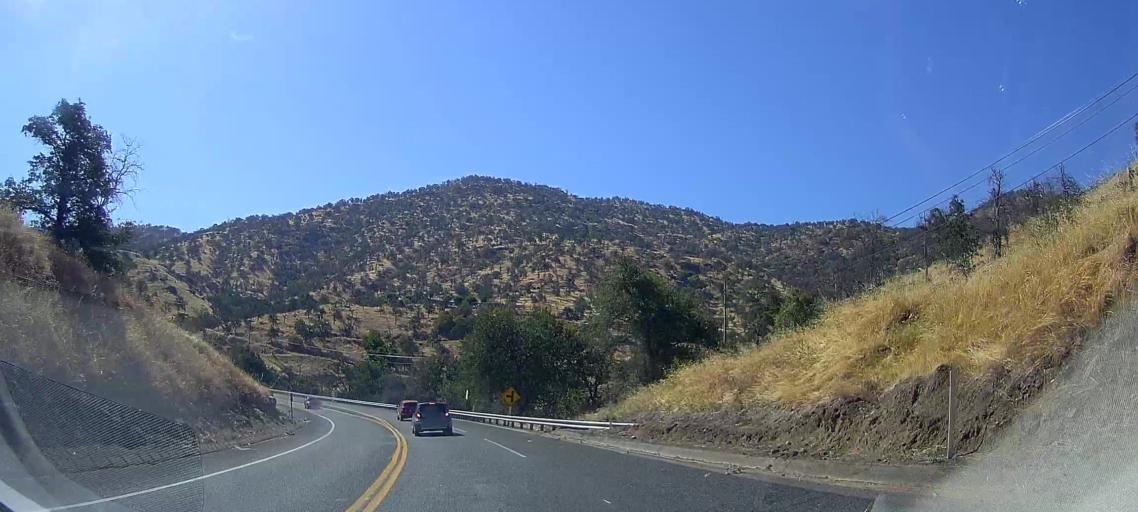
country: US
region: California
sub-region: Tulare County
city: Three Rivers
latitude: 36.3960
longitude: -118.9899
